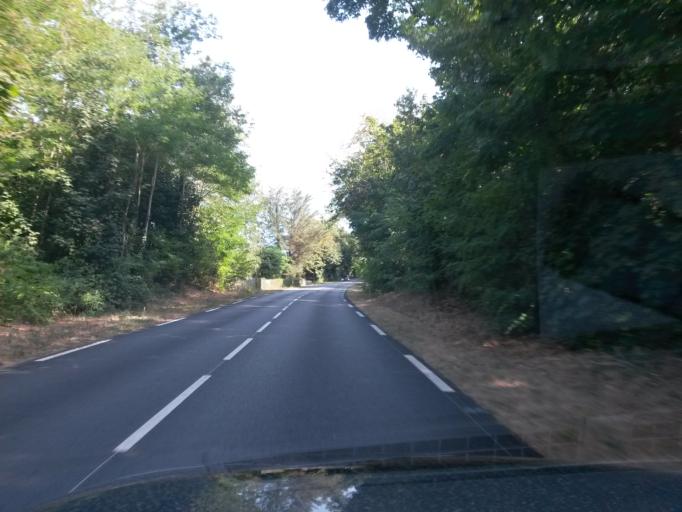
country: FR
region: Pays de la Loire
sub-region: Departement de la Vendee
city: Olonne-sur-Mer
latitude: 46.5613
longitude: -1.8127
